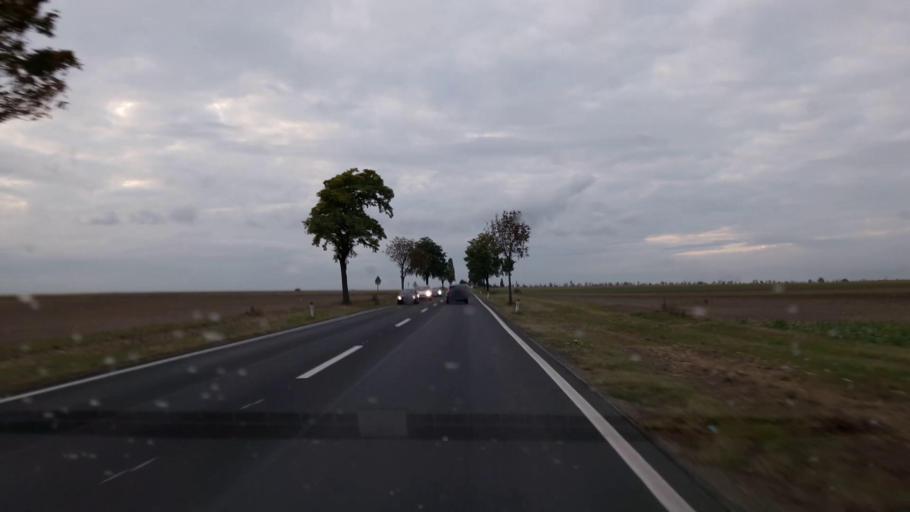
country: AT
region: Lower Austria
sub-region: Politischer Bezirk Wien-Umgebung
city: Schwadorf
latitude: 48.0859
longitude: 16.5607
